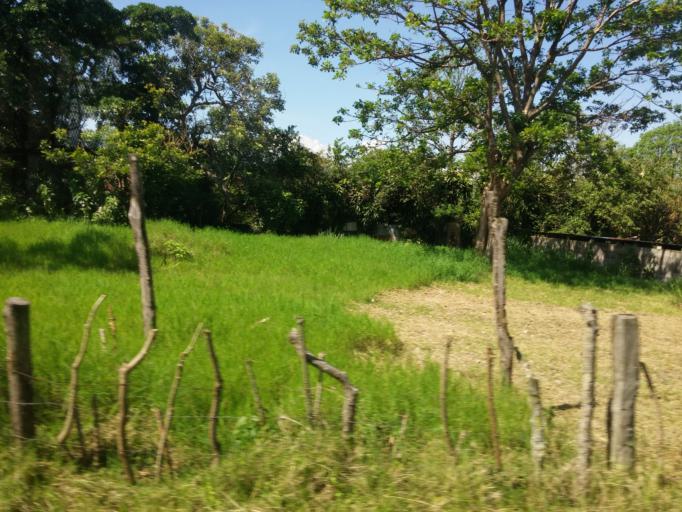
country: CR
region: Heredia
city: Mercedes
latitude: 9.9994
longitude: -84.1401
